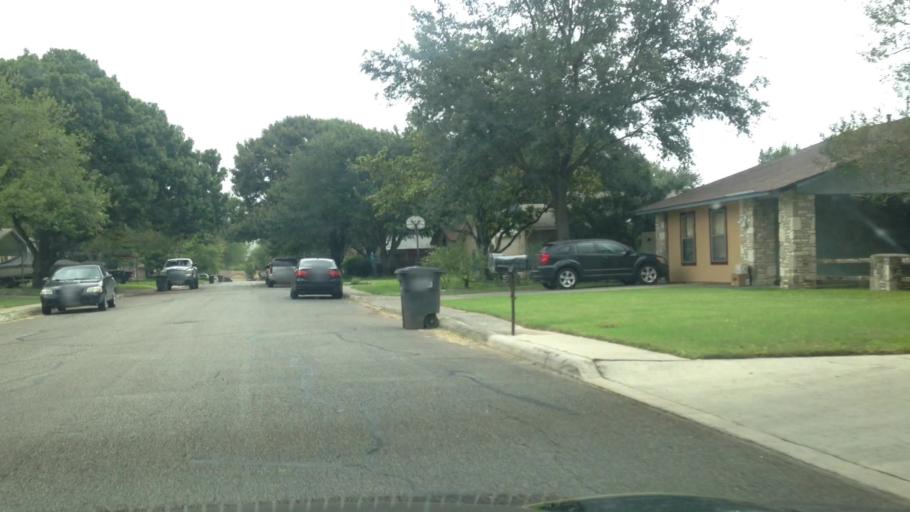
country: US
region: Texas
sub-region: Bexar County
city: Windcrest
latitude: 29.5750
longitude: -98.4145
